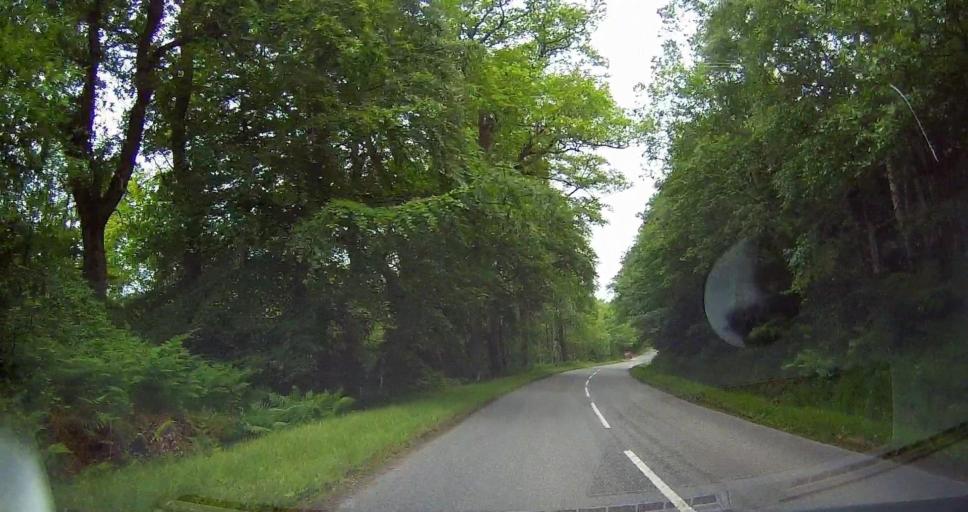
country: GB
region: Scotland
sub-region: Highland
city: Dornoch
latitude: 57.9596
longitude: -4.0741
